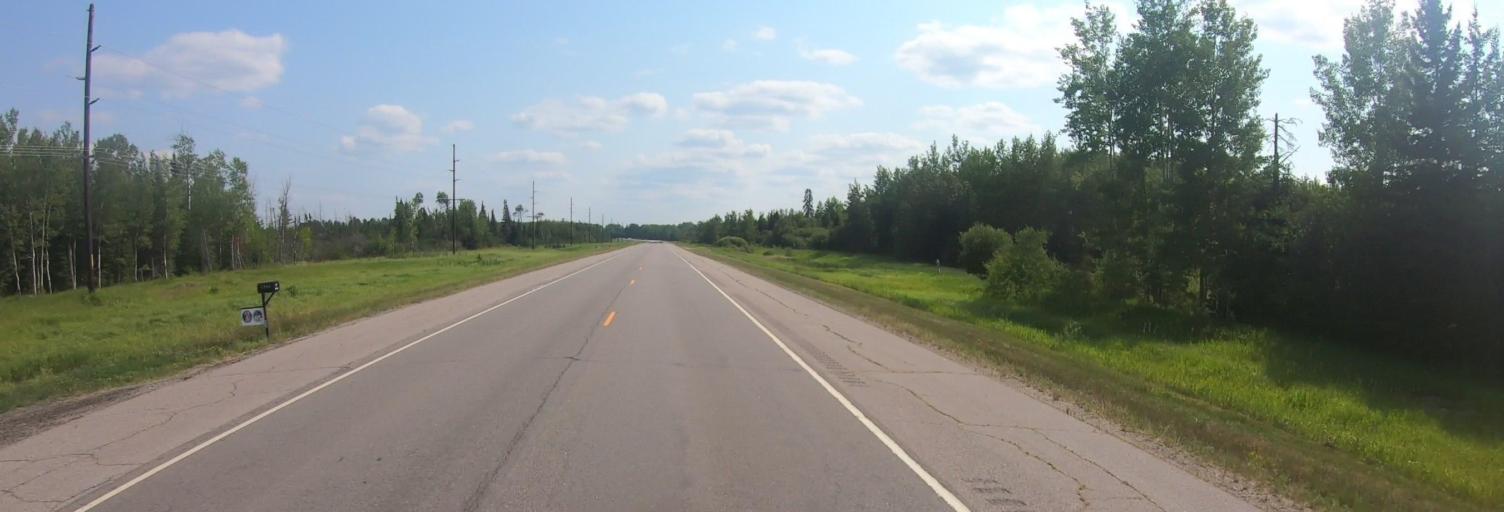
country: US
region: Minnesota
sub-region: Saint Louis County
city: Chisholm
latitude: 47.9378
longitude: -92.8287
